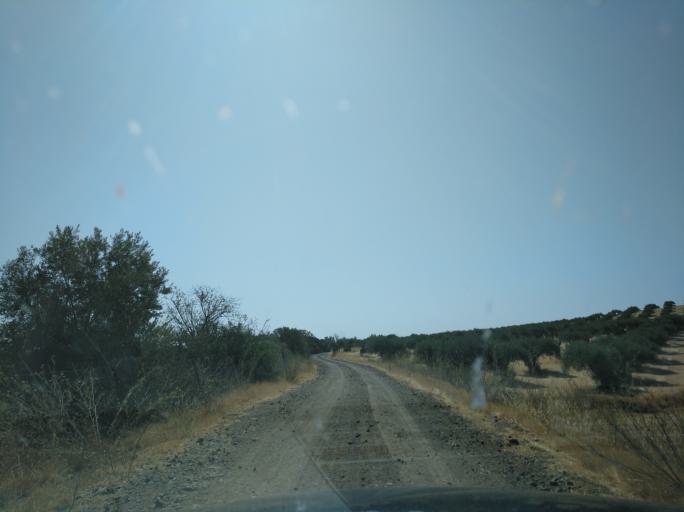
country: PT
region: Portalegre
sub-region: Campo Maior
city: Campo Maior
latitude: 39.0698
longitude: -7.0157
